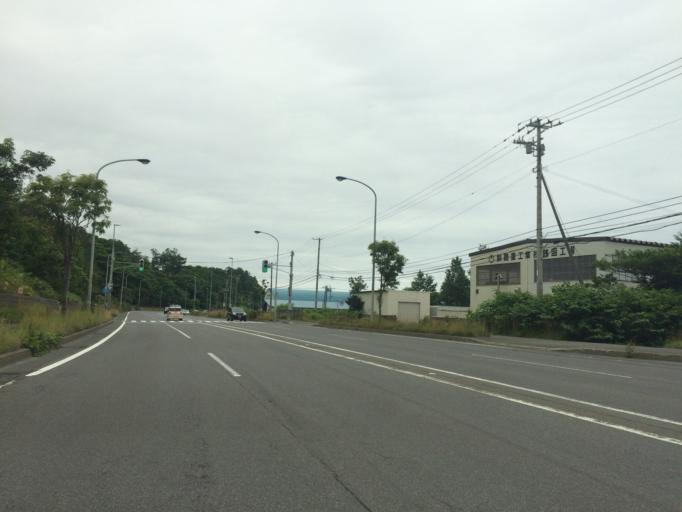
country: JP
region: Hokkaido
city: Otaru
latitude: 43.1358
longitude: 141.1732
